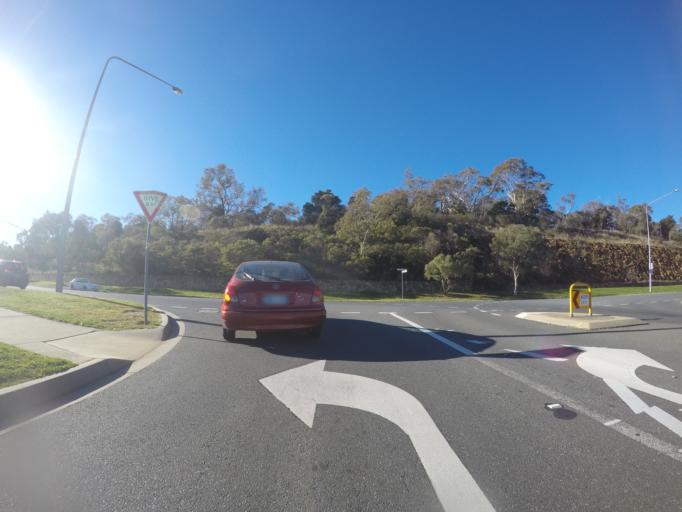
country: AU
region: Australian Capital Territory
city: Canberra
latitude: -35.2954
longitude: 149.1508
